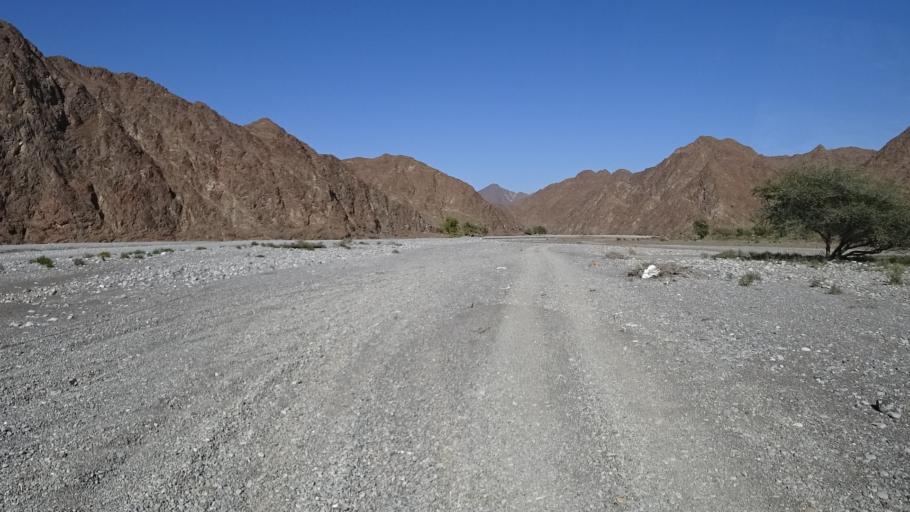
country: OM
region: Al Batinah
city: Bayt al `Awabi
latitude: 23.3983
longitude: 57.6637
